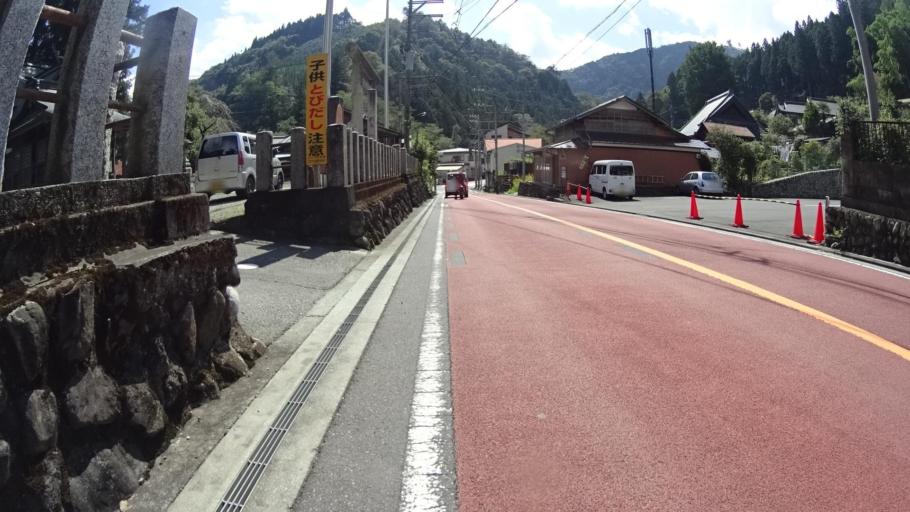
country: JP
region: Tokyo
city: Itsukaichi
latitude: 35.7273
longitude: 139.1467
